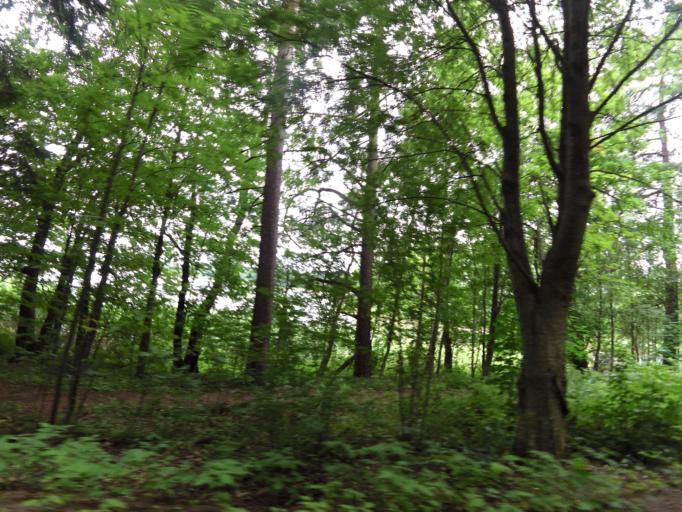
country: FI
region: Uusimaa
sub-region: Helsinki
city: Otaniemi
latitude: 60.1744
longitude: 24.8226
